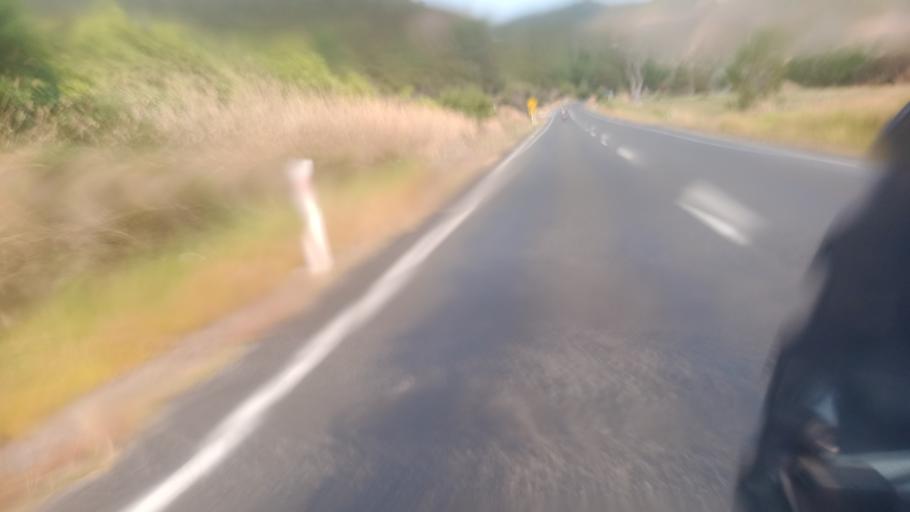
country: NZ
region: Bay of Plenty
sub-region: Opotiki District
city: Opotiki
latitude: -37.7957
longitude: 177.6612
